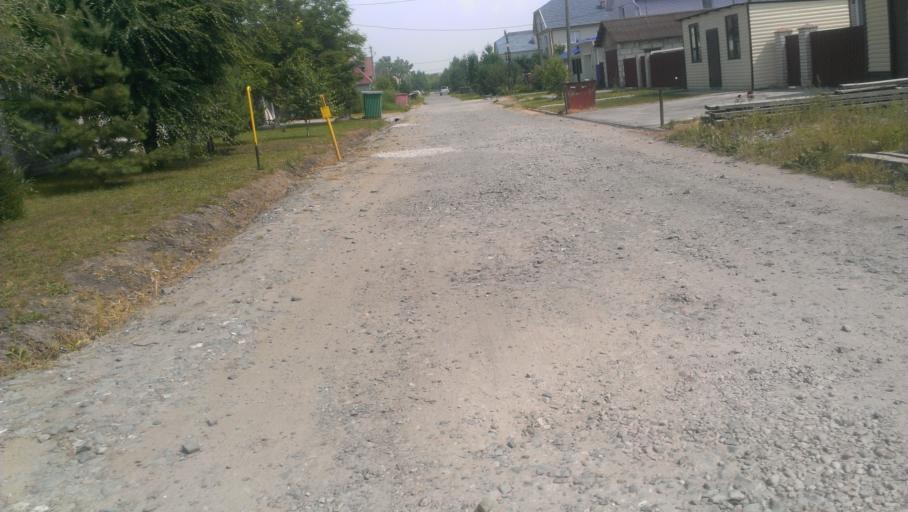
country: RU
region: Altai Krai
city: Novosilikatnyy
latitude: 53.3491
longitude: 83.6415
